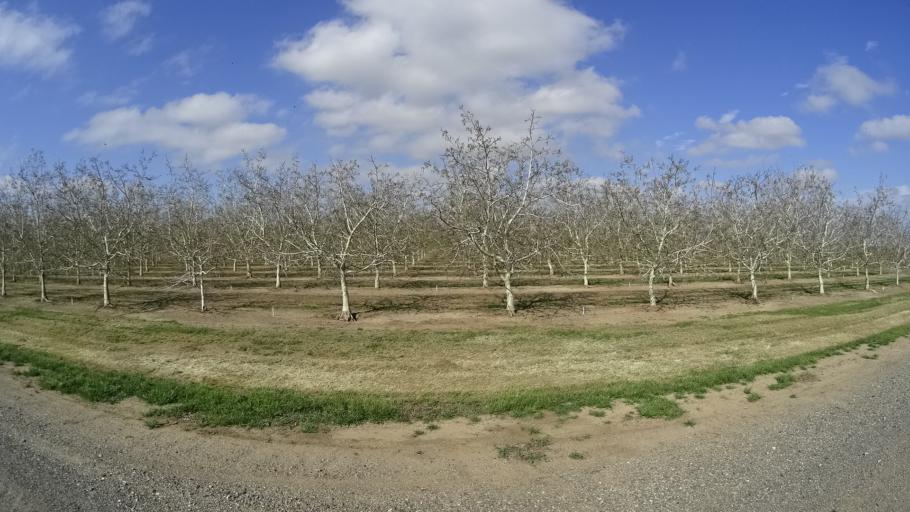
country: US
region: California
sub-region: Butte County
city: Biggs
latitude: 39.4492
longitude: -121.9304
